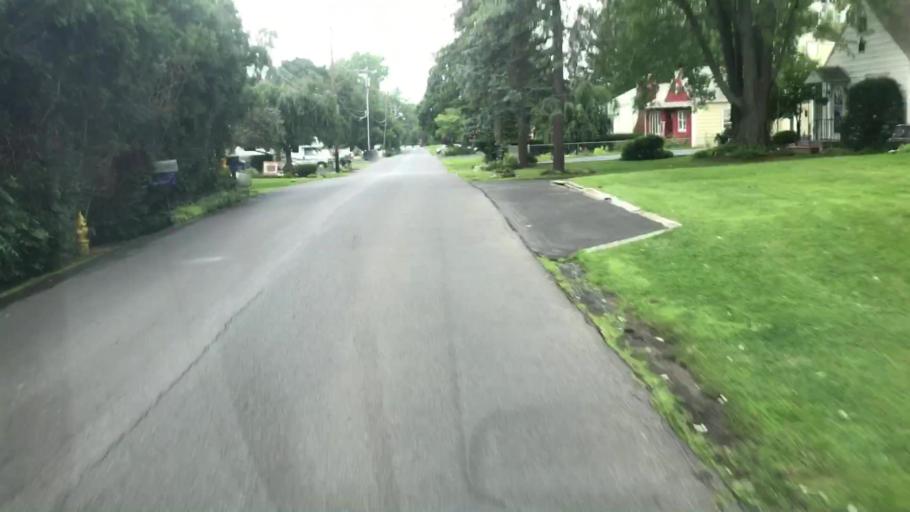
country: US
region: New York
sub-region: Cayuga County
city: Melrose Park
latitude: 42.9124
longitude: -76.5396
